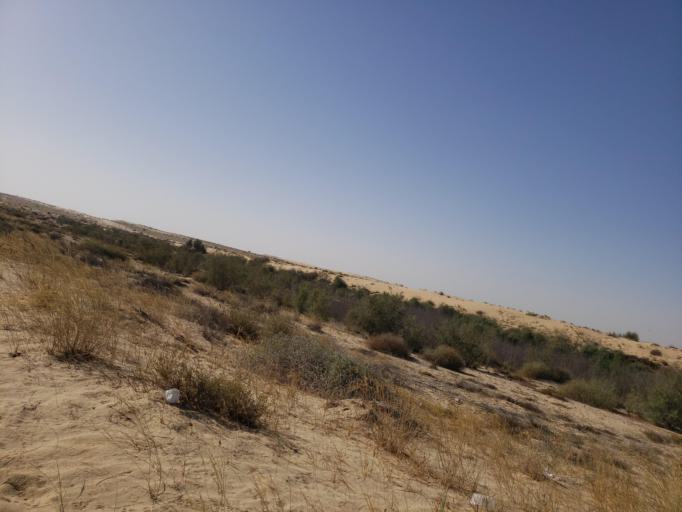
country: AE
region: Dubai
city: Dubai
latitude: 24.9710
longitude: 55.2122
